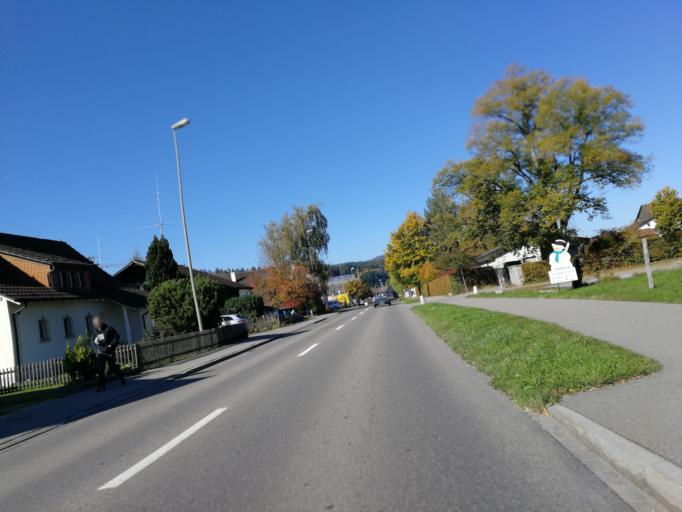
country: CH
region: Zurich
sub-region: Bezirk Meilen
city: Oetwil am See
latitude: 47.2691
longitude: 8.7237
